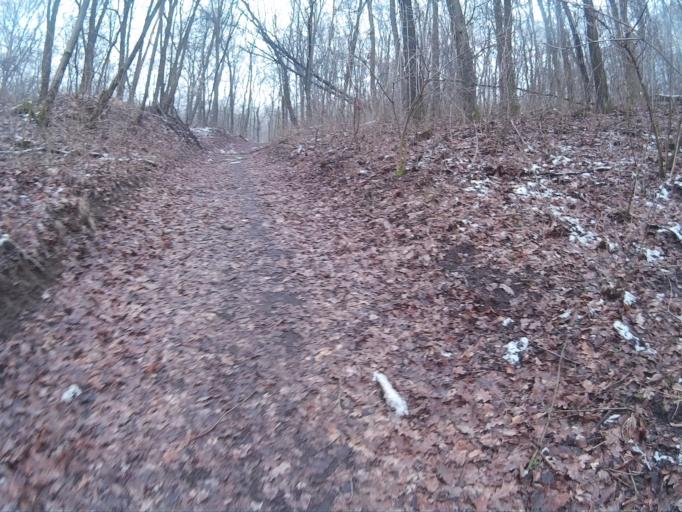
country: HU
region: Komarom-Esztergom
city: Tarjan
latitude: 47.5940
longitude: 18.5139
